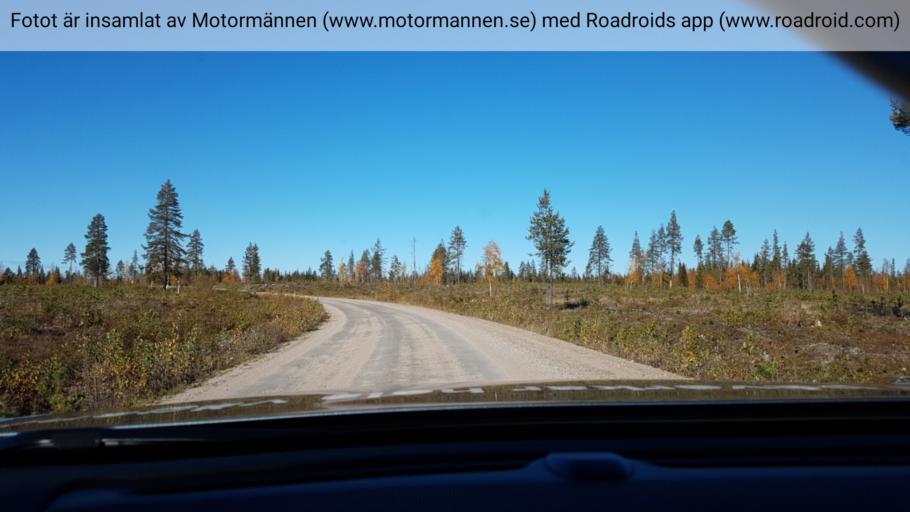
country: SE
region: Norrbotten
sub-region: Gallivare Kommun
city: Gaellivare
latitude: 66.6561
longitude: 20.9867
